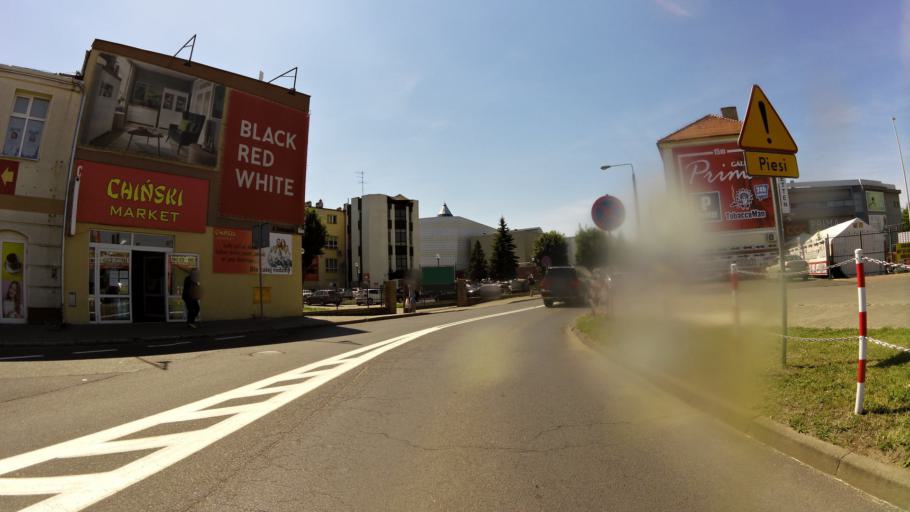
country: PL
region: Lubusz
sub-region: Powiat slubicki
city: Slubice
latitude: 52.3487
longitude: 14.5617
